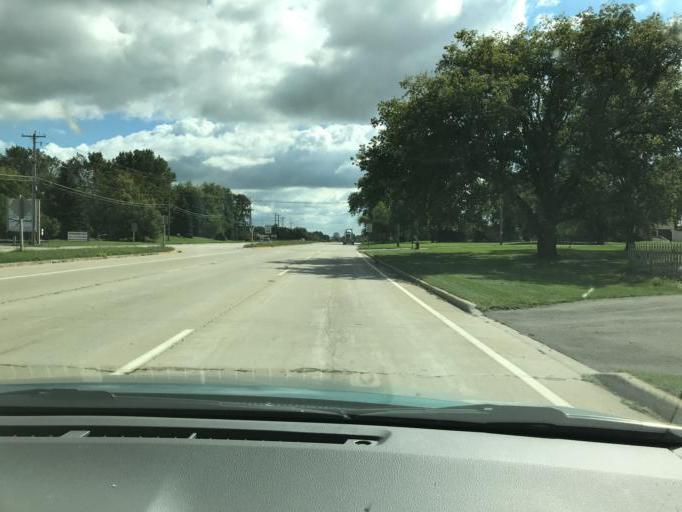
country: US
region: Wisconsin
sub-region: Kenosha County
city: Pleasant Prairie
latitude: 42.5622
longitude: -87.8889
